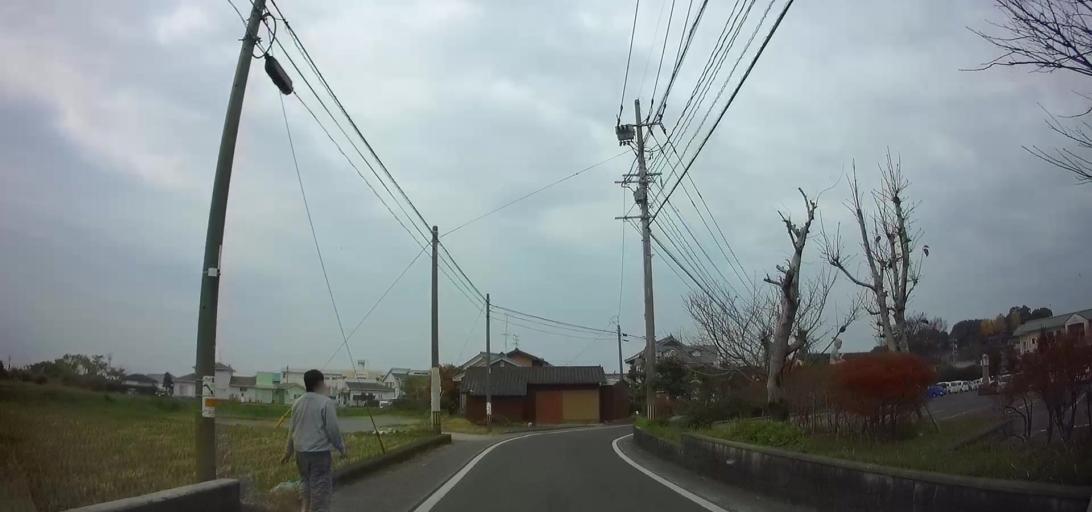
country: JP
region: Nagasaki
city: Shimabara
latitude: 32.6595
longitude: 130.2982
